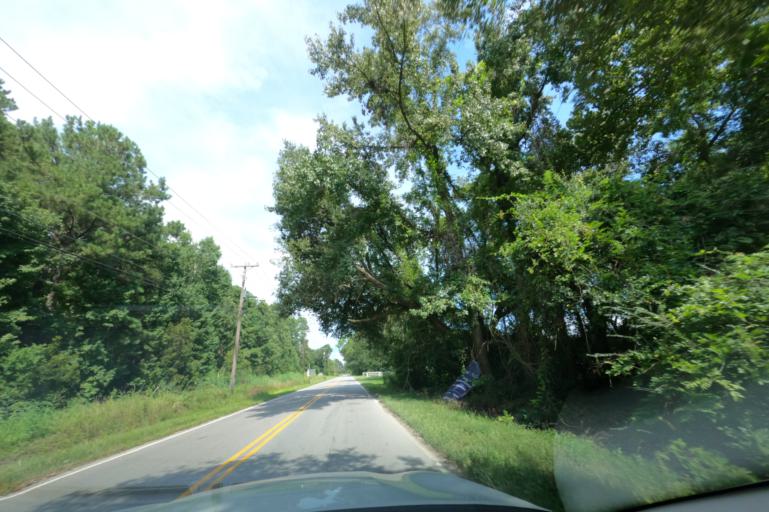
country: US
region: South Carolina
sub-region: Charleston County
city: Shell Point
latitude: 32.8020
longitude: -80.1202
